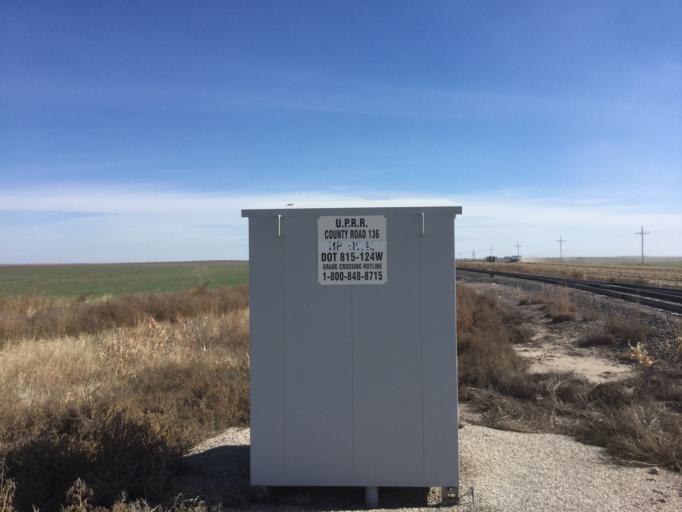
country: US
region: Kansas
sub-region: Trego County
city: WaKeeney
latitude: 39.0104
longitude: -99.8346
